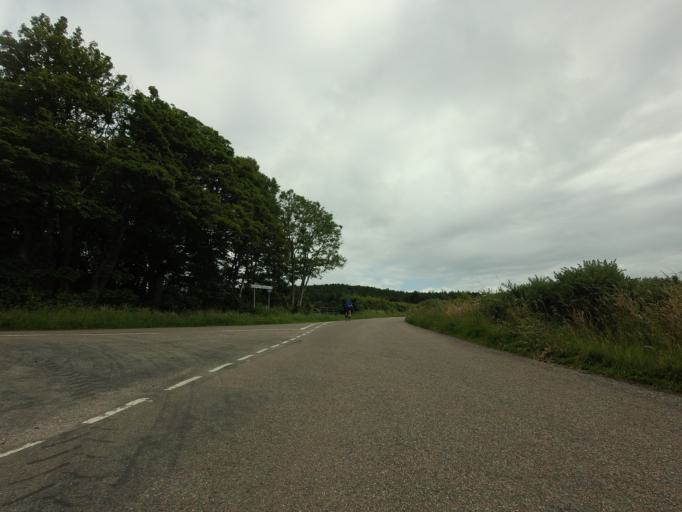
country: GB
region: Scotland
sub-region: Moray
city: Lhanbryd
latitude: 57.6668
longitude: -3.1711
